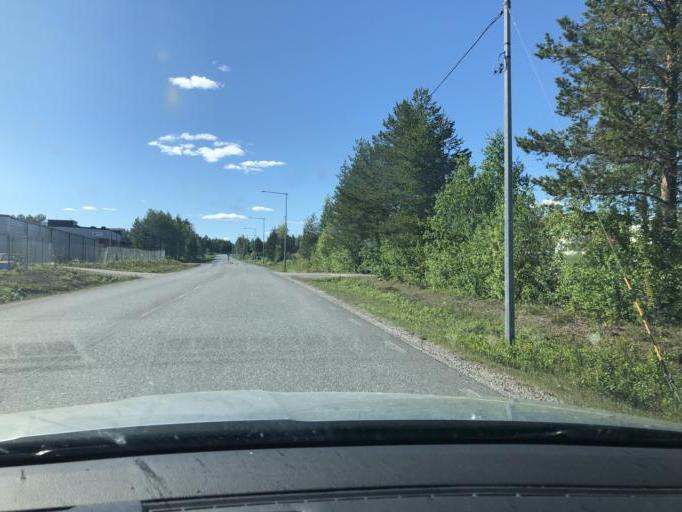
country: SE
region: Norrbotten
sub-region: Kalix Kommun
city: Kalix
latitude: 65.8575
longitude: 23.1725
